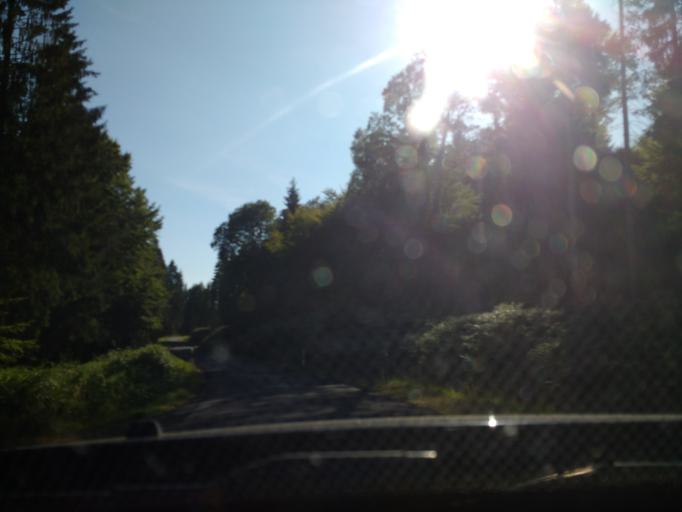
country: DE
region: Rheinland-Pfalz
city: Meisburg
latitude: 50.1287
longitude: 6.6541
